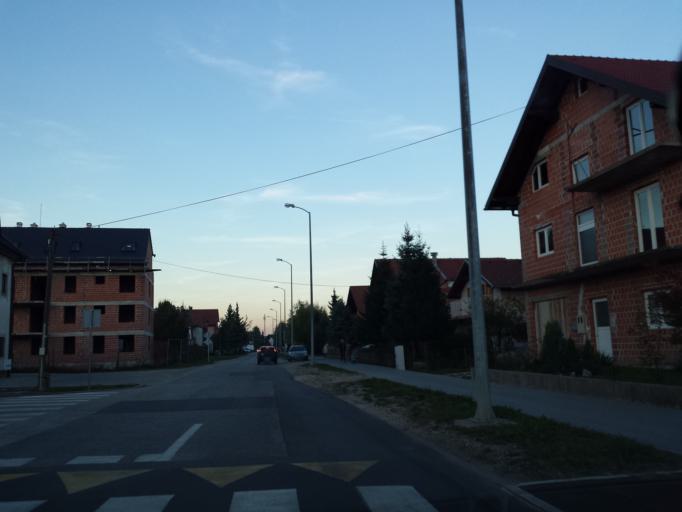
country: HR
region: Zagrebacka
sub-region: Grad Samobor
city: Samobor
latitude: 45.7971
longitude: 15.7294
